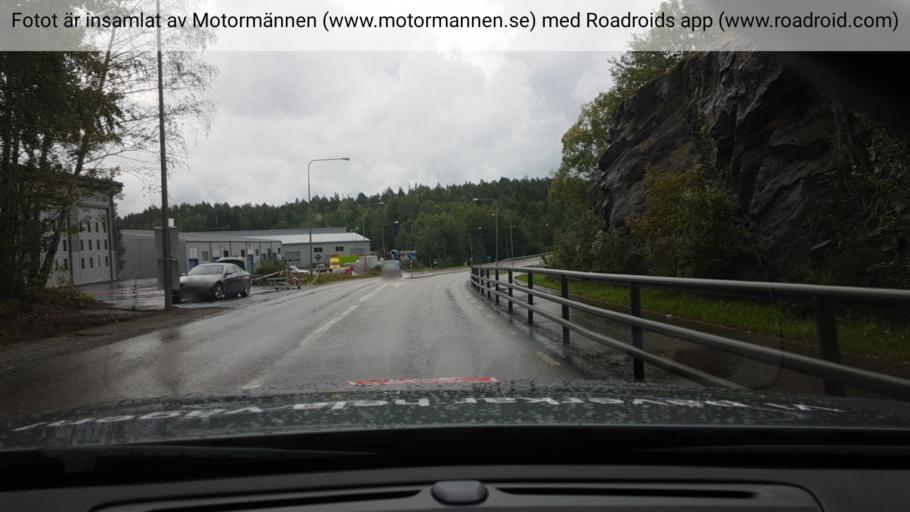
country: SE
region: Stockholm
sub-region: Botkyrka Kommun
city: Tullinge
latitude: 59.2079
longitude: 17.9219
